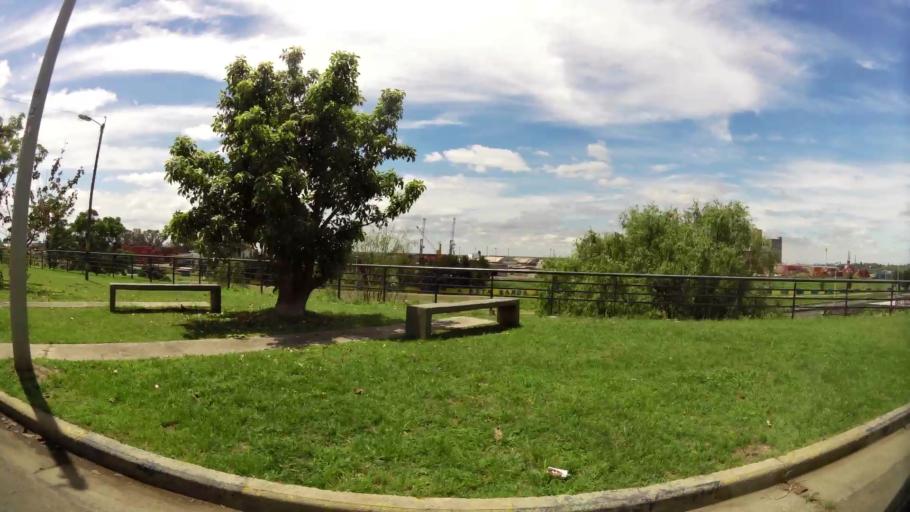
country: AR
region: Santa Fe
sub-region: Departamento de Rosario
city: Rosario
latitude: -32.9762
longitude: -60.6253
